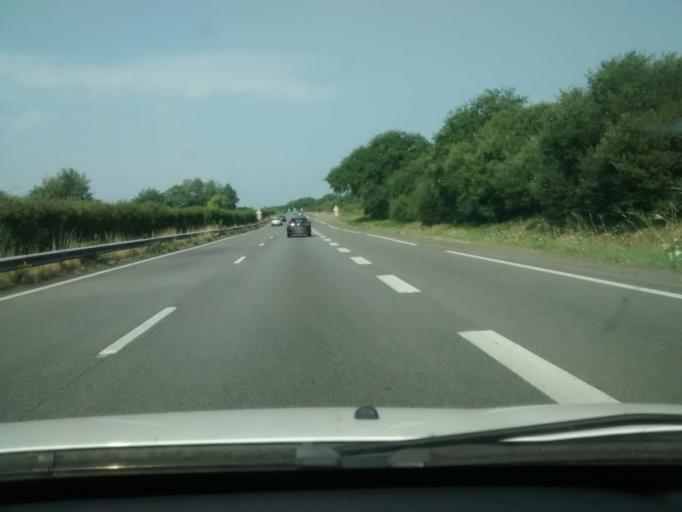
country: FR
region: Pays de la Loire
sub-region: Departement de la Loire-Atlantique
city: Prinquiau
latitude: 47.3588
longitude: -2.0362
